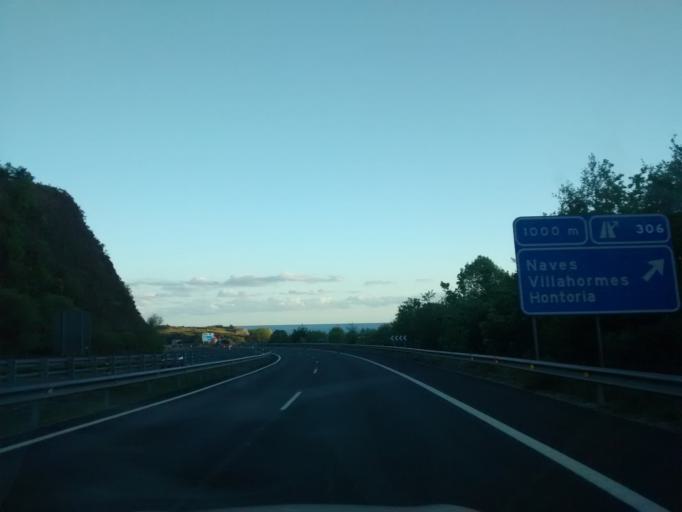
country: ES
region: Asturias
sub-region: Province of Asturias
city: Llanes
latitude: 43.4392
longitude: -4.8722
